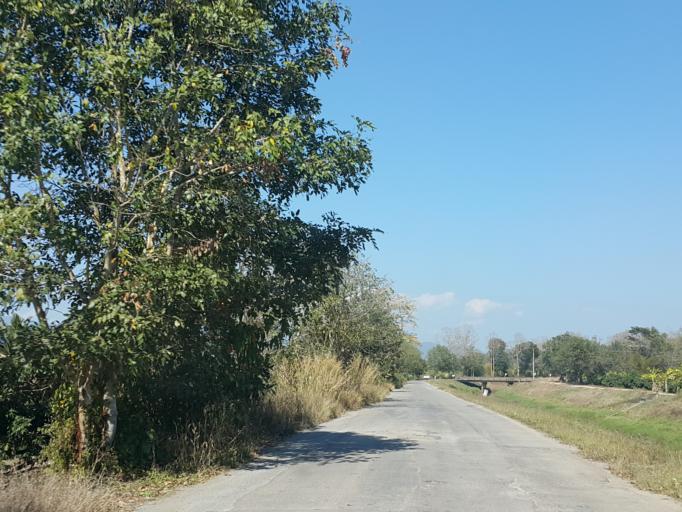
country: TH
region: Chiang Mai
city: Mae Taeng
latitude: 19.0886
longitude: 98.9501
